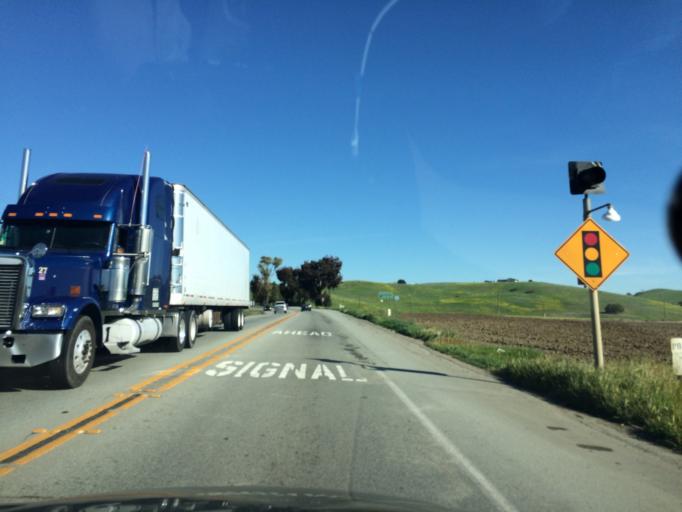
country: US
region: California
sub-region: San Benito County
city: Hollister
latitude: 36.8417
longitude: -121.4612
